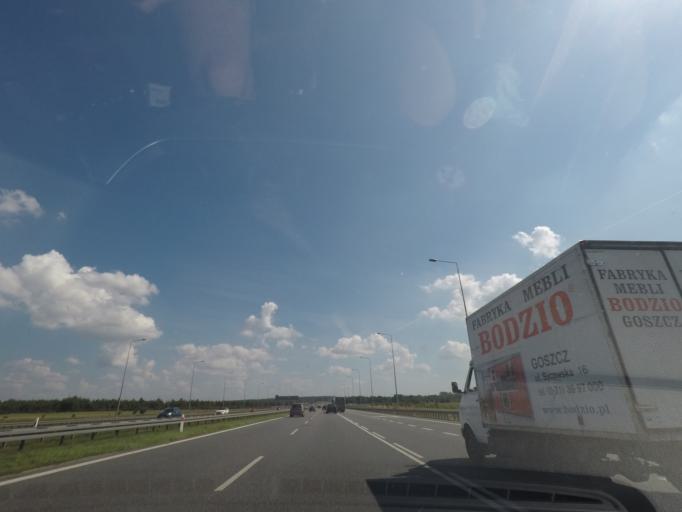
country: PL
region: Lodz Voivodeship
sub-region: Powiat zgierski
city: Strykow
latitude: 51.8830
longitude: 19.6427
